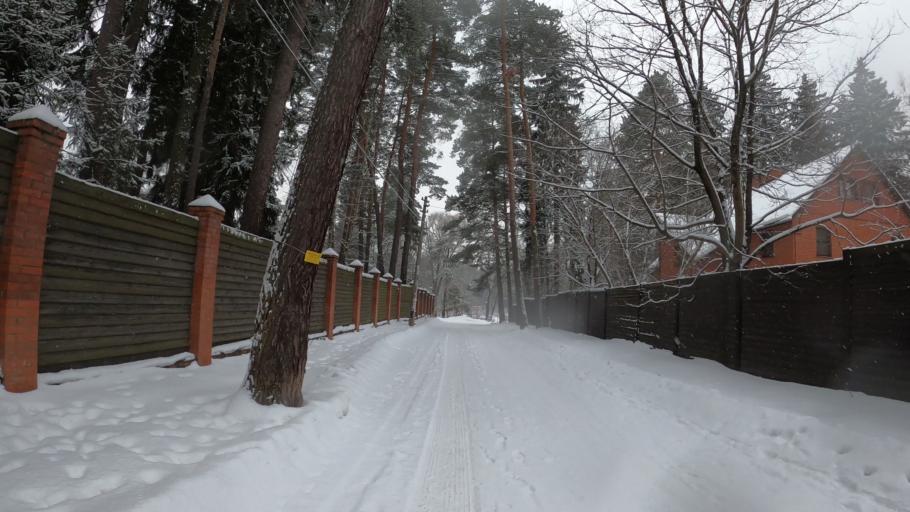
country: RU
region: Moskovskaya
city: Kratovo
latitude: 55.5870
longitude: 38.1650
